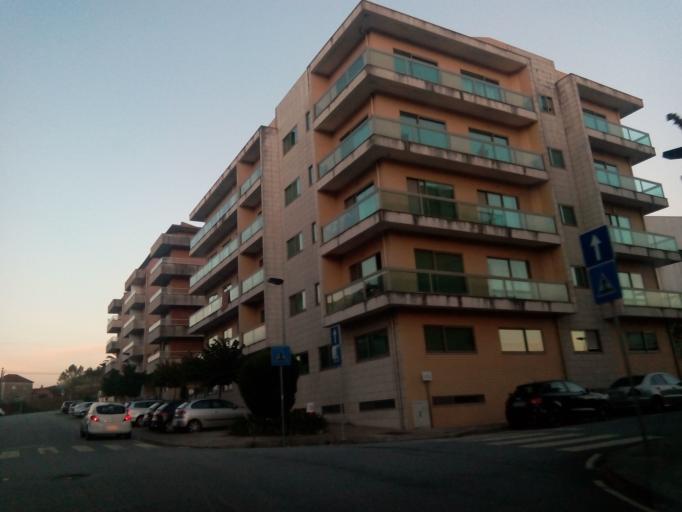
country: PT
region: Porto
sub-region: Paredes
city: Gandra
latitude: 41.1830
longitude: -8.4399
